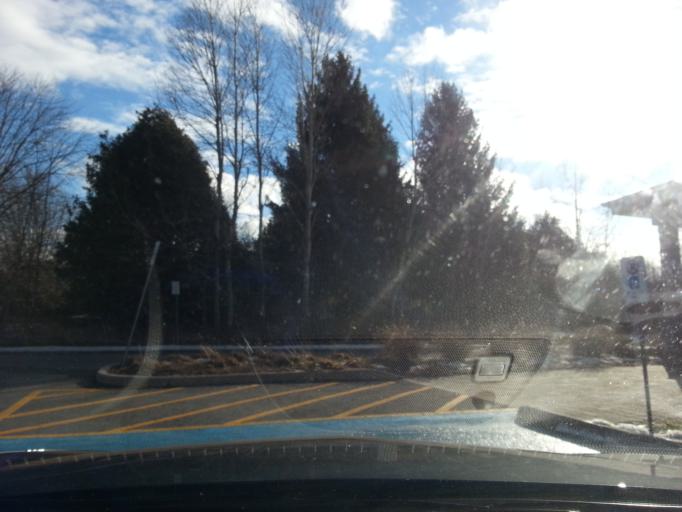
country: CA
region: Ontario
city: Bells Corners
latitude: 45.0287
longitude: -75.6601
